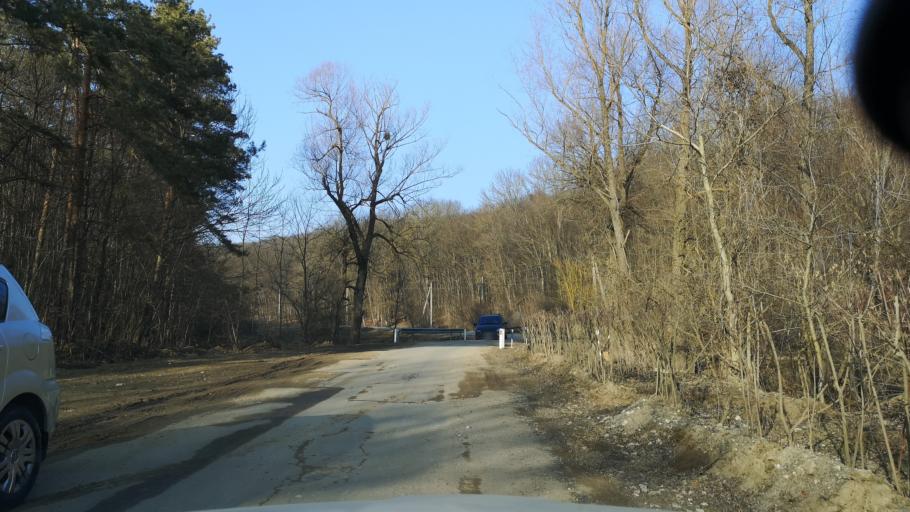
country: MD
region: Nisporeni
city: Nisporeni
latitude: 47.0834
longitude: 28.3220
